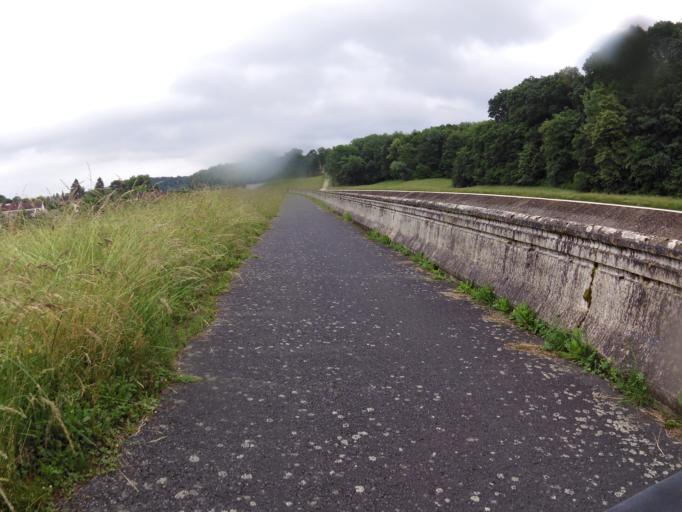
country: FR
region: Champagne-Ardenne
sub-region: Departement de la Haute-Marne
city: Saint-Dizier
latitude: 48.6153
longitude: 4.9022
